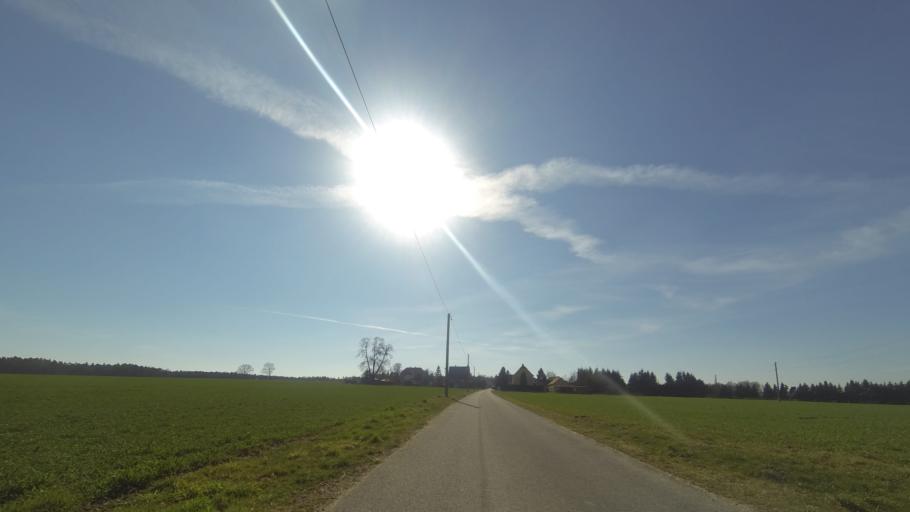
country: DE
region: Saxony
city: Tauscha
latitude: 51.2360
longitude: 13.8017
